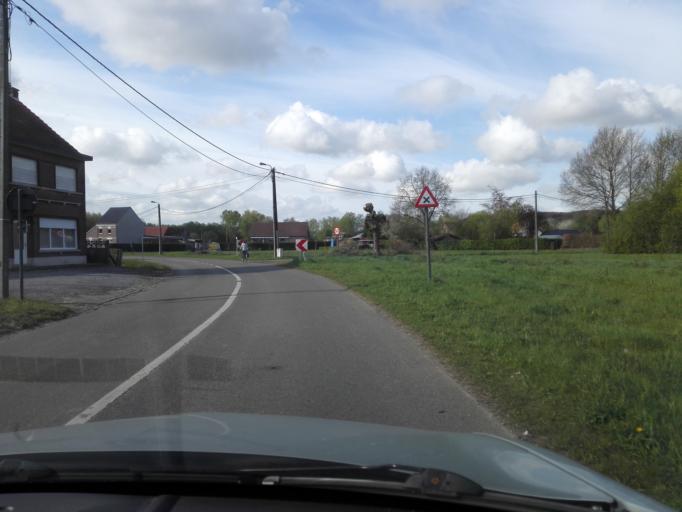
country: BE
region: Flanders
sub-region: Provincie Vlaams-Brabant
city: Aarschot
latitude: 50.9581
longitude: 4.8968
